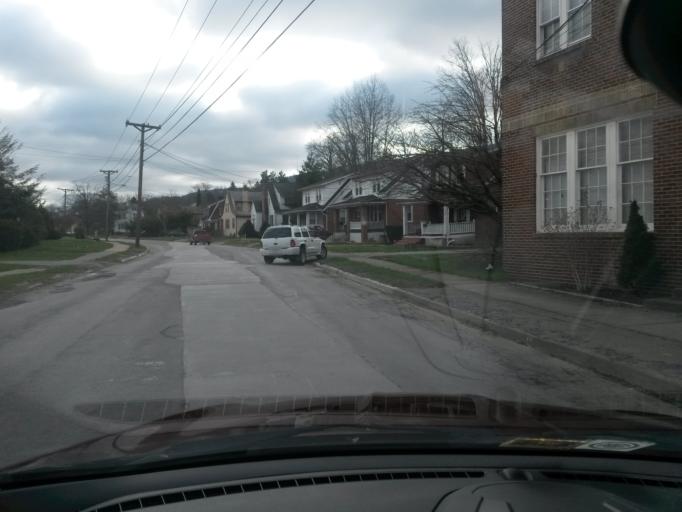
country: US
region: West Virginia
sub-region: Mercer County
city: Bluefield
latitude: 37.2504
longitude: -81.2313
